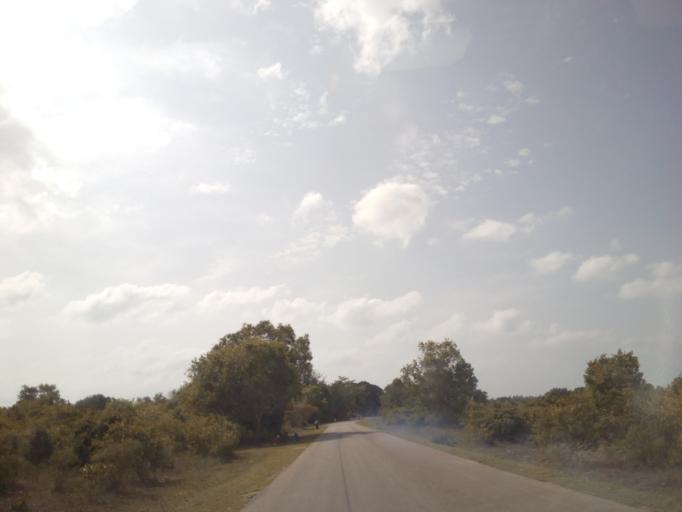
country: TZ
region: Zanzibar Central/South
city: Koani
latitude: -6.2833
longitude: 39.3681
